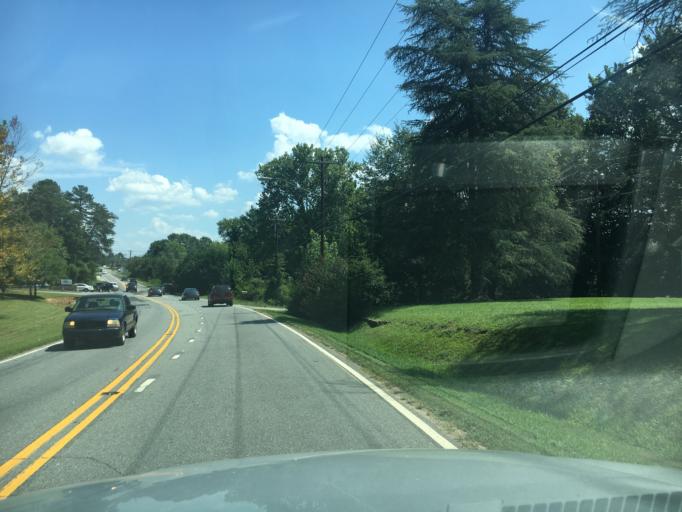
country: US
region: North Carolina
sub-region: Rutherford County
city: Forest City
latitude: 35.3004
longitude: -81.8538
